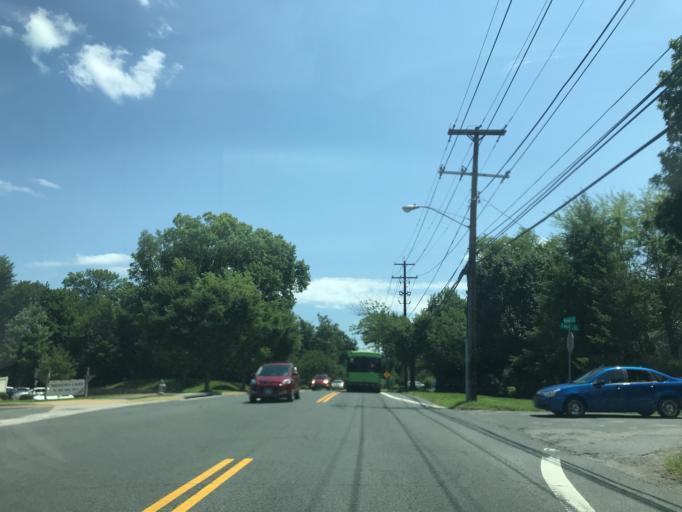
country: US
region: Maryland
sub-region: Montgomery County
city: Kensington
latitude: 39.0298
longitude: -77.0837
